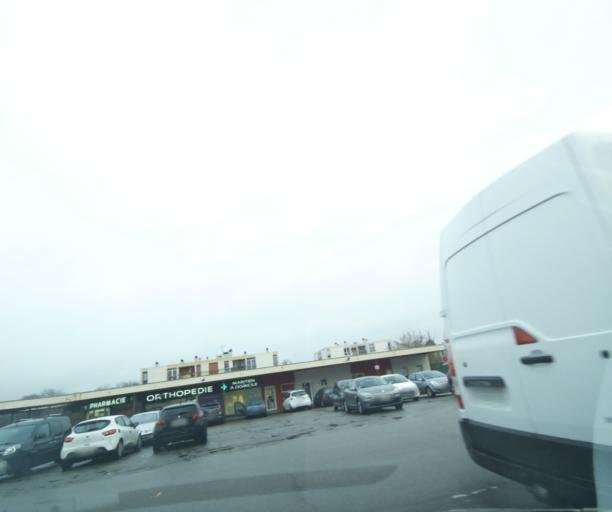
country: FR
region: Ile-de-France
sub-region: Departement de Seine-et-Marne
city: Avon
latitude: 48.4120
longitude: 2.7366
